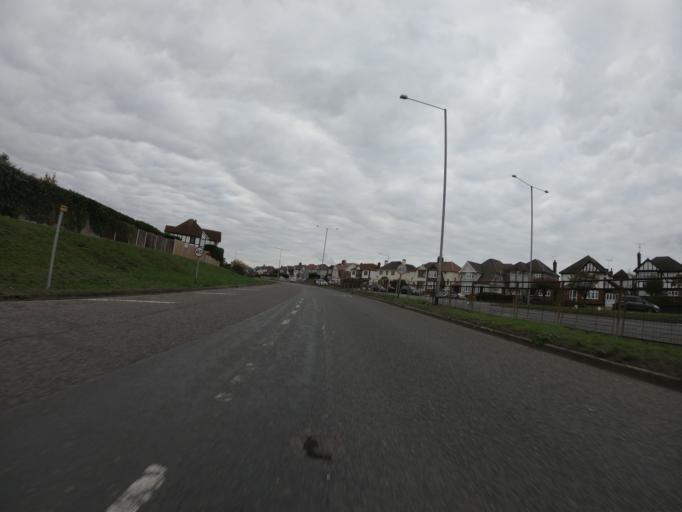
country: GB
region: England
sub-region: Borough of Thurrock
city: Chadwell St Mary
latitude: 51.4864
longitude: 0.3484
